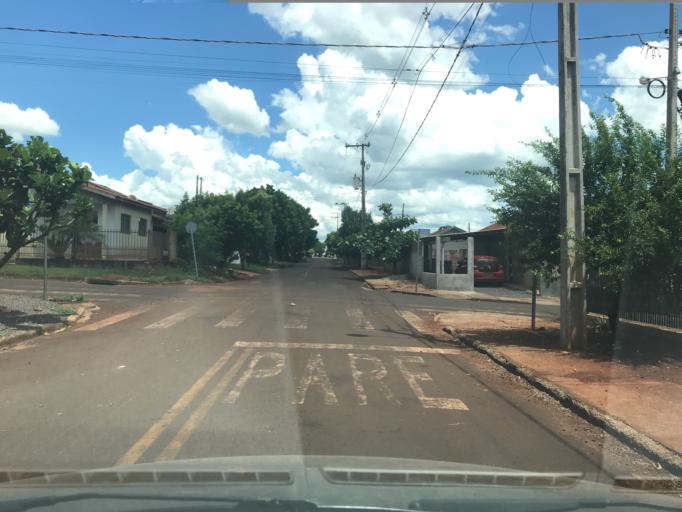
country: BR
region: Parana
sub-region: Palotina
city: Palotina
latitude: -24.2673
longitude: -53.8463
